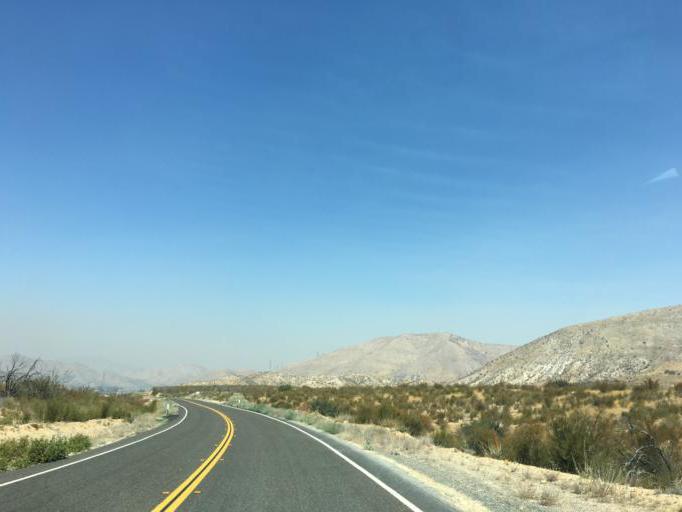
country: US
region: California
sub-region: Los Angeles County
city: Vincent
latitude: 34.4262
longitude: -118.1068
